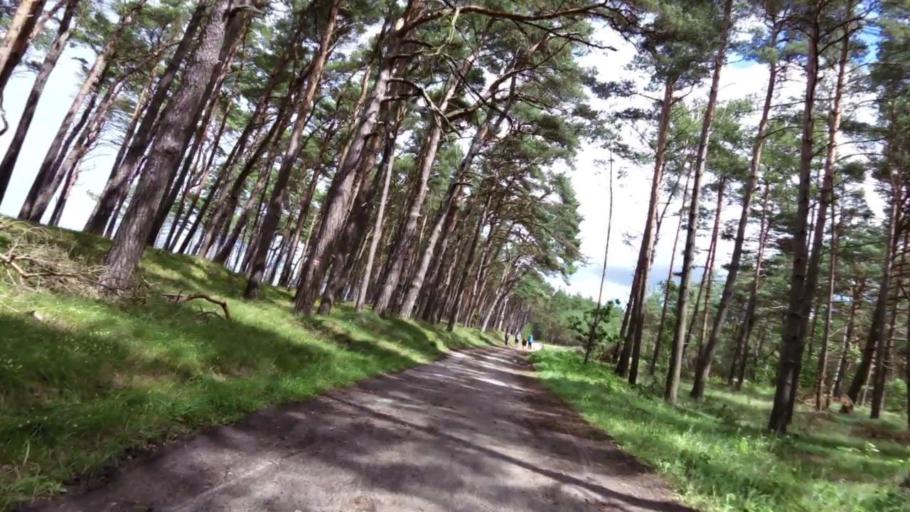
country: PL
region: West Pomeranian Voivodeship
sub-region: Powiat slawienski
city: Darlowo
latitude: 54.4980
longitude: 16.4509
